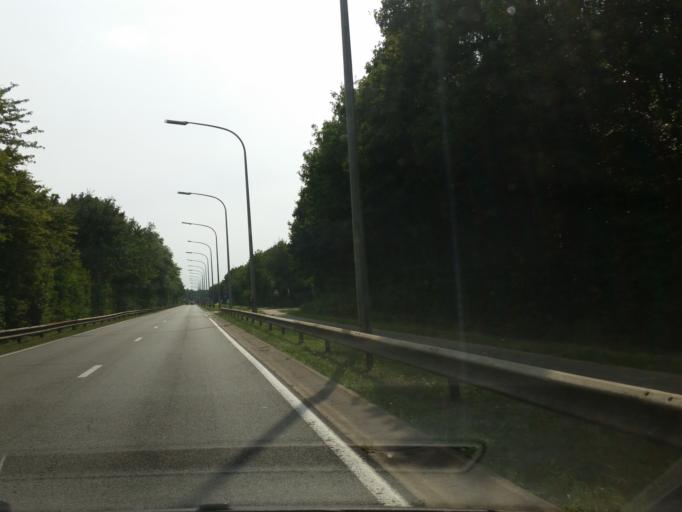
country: BE
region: Flanders
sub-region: Provincie Vlaams-Brabant
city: Machelen
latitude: 50.9199
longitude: 4.4407
